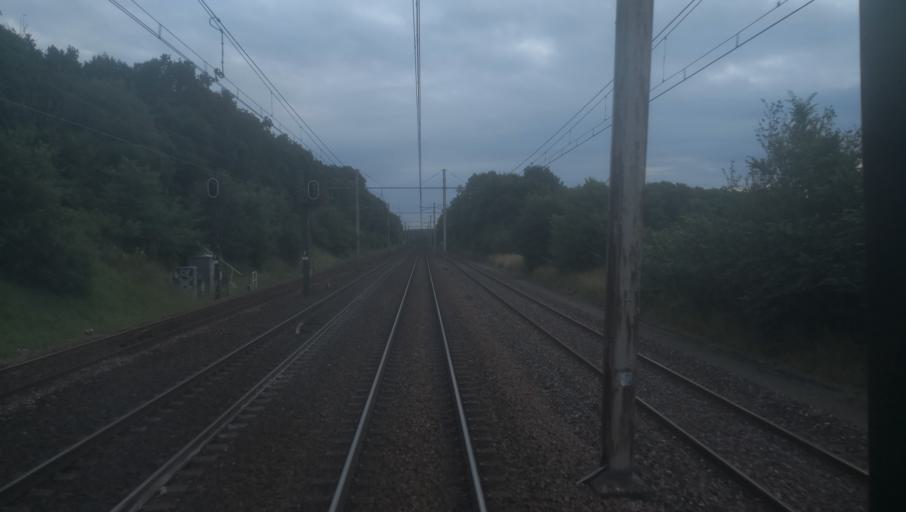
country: FR
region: Ile-de-France
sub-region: Departement de l'Essonne
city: Morigny-Champigny
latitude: 48.4690
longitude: 2.1828
